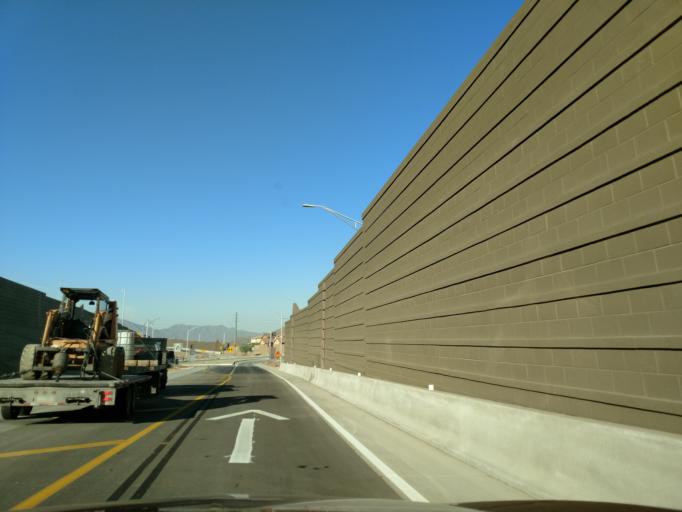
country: US
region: Arizona
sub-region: Maricopa County
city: Laveen
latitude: 33.2920
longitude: -112.0955
